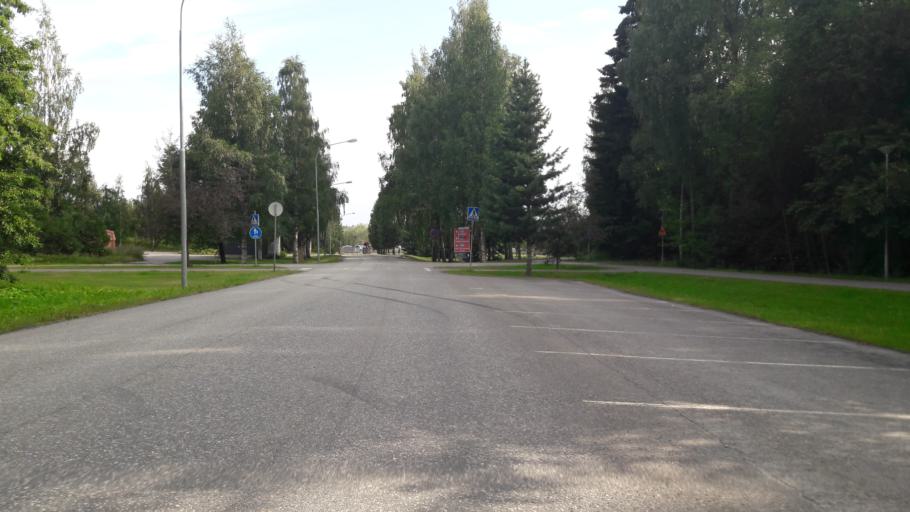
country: FI
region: North Karelia
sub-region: Joensuu
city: Joensuu
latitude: 62.5932
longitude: 29.7405
